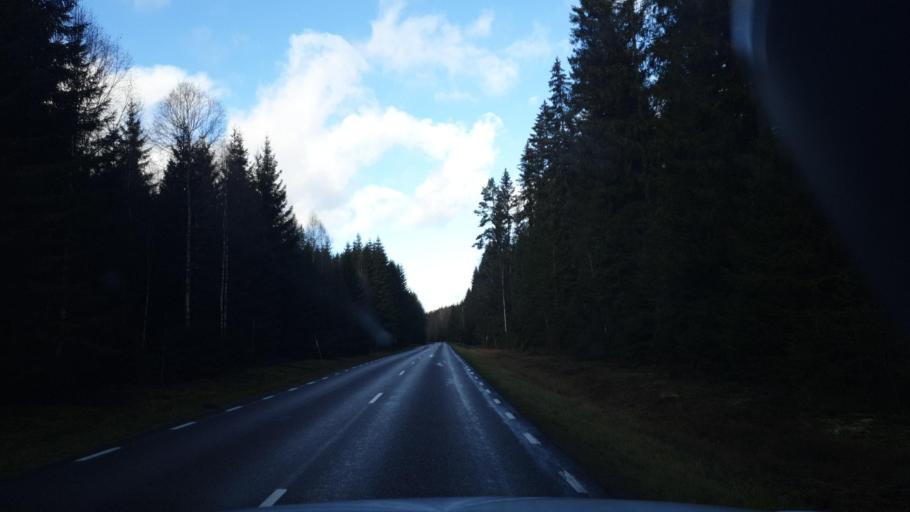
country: SE
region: Vaermland
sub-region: Grums Kommun
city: Slottsbron
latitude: 59.4597
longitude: 12.8346
